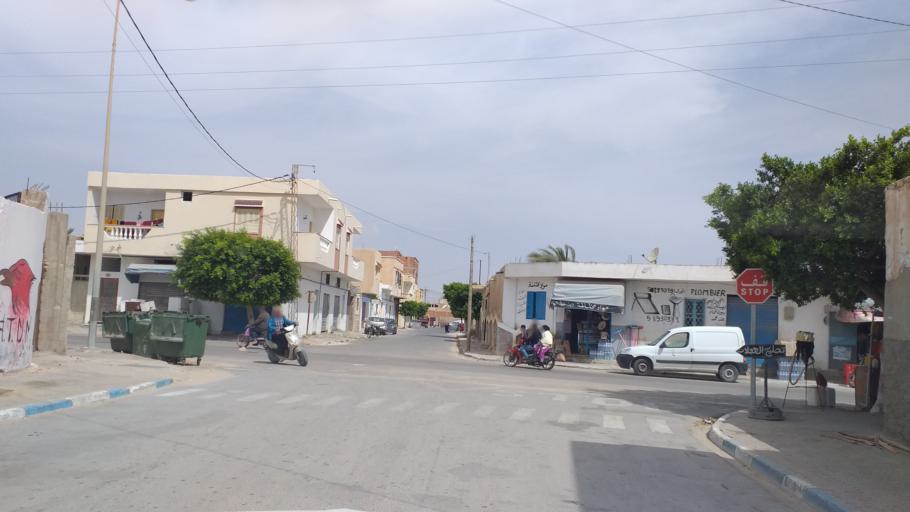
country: TN
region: Qabis
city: Gabes
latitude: 33.9388
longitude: 10.0622
